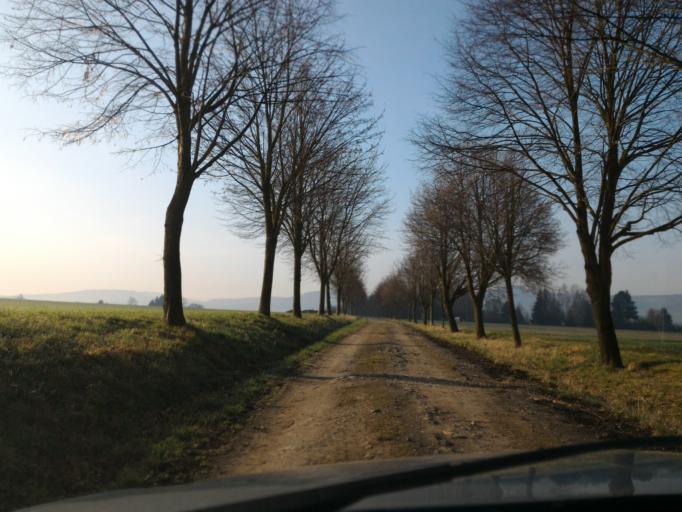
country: DE
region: Saxony
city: Grossschonau
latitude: 50.9120
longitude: 14.6661
